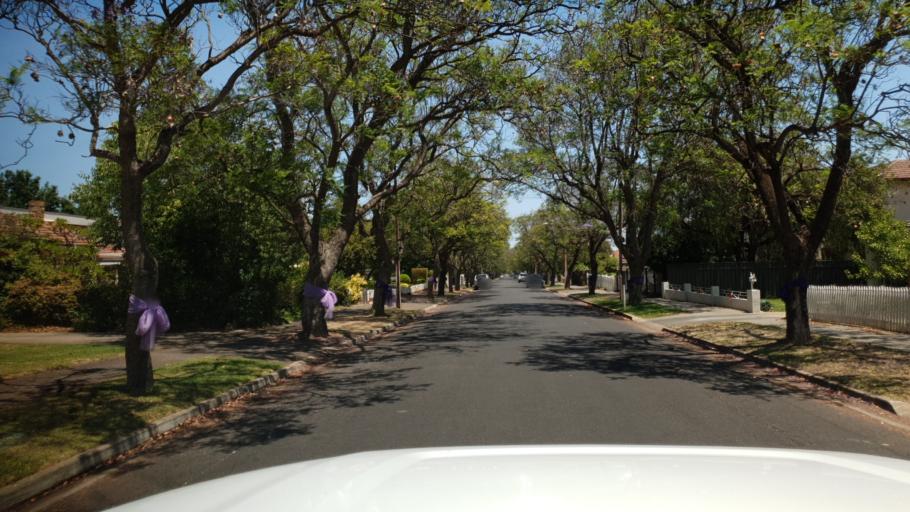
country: AU
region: South Australia
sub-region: Mitcham
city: Clarence Gardens
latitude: -34.9752
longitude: 138.5883
